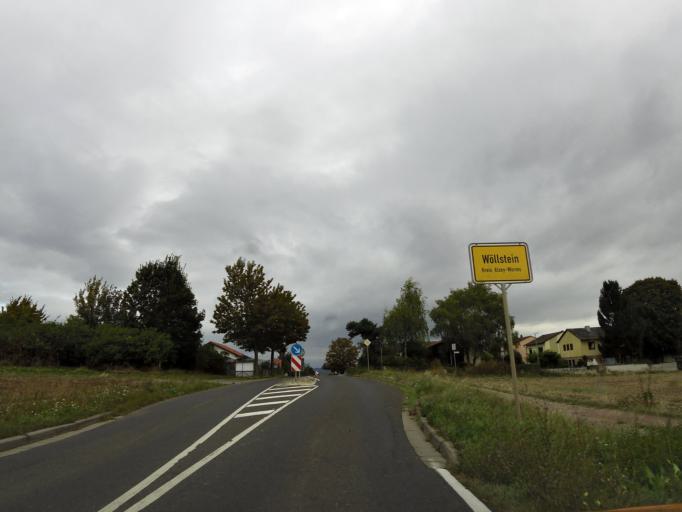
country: DE
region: Rheinland-Pfalz
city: Siefersheim
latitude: 49.8053
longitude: 7.9585
